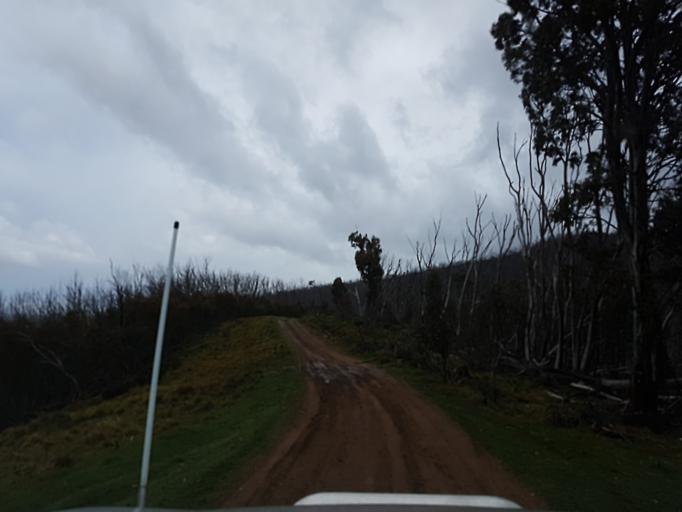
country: AU
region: Victoria
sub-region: Alpine
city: Mount Beauty
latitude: -37.0903
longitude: 147.0987
